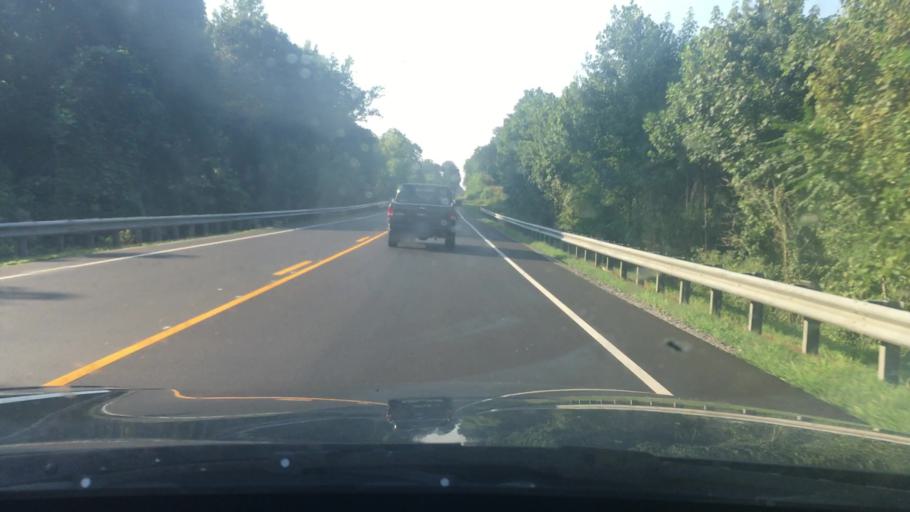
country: US
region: North Carolina
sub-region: Caswell County
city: Yanceyville
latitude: 36.4420
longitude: -79.3635
